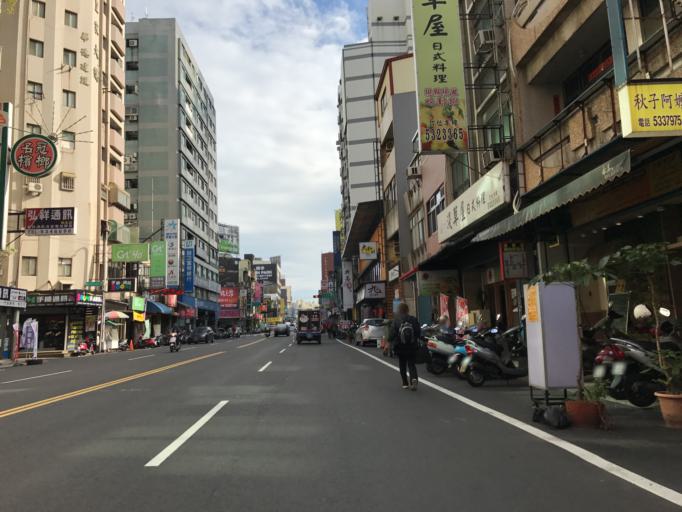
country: TW
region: Taiwan
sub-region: Hsinchu
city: Hsinchu
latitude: 24.8106
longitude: 120.9767
